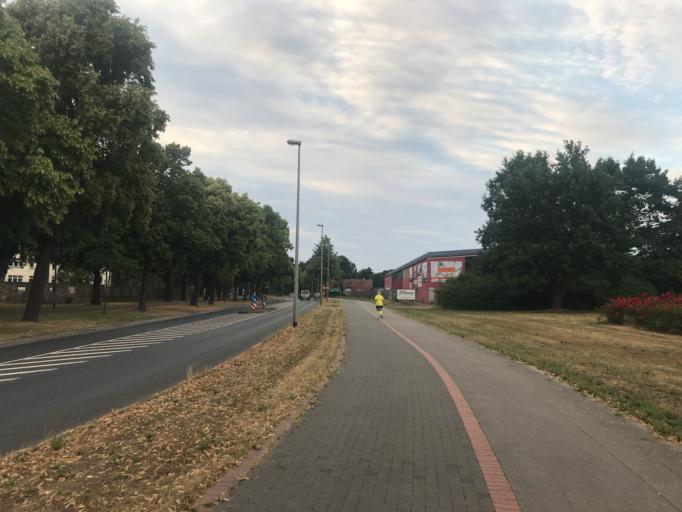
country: DE
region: Lower Saxony
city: Langenhagen
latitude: 52.4179
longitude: 9.7931
